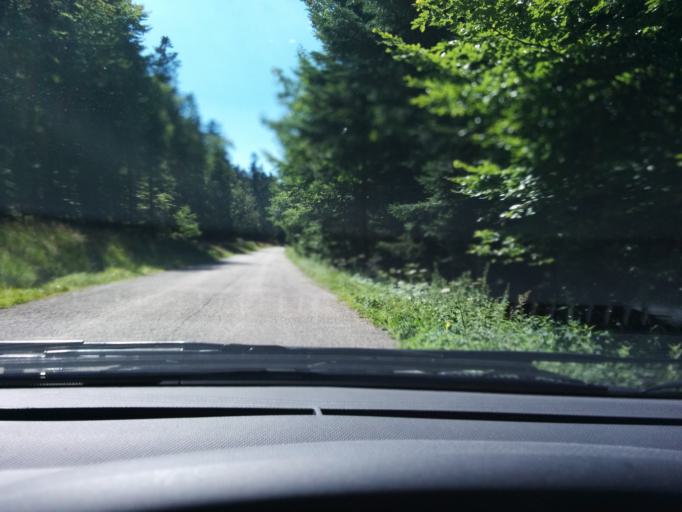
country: AT
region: Upper Austria
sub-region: Politischer Bezirk Rohrbach
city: Ulrichsberg
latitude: 48.6987
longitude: 13.9450
